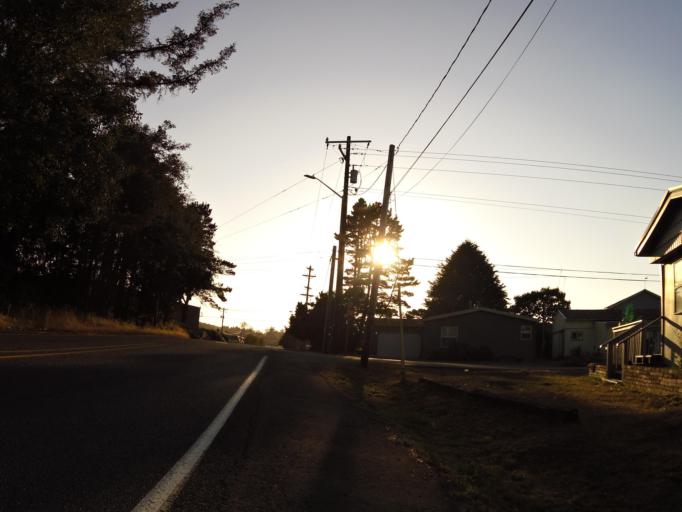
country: US
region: Oregon
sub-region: Lincoln County
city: Lincoln City
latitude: 44.9609
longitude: -124.0071
